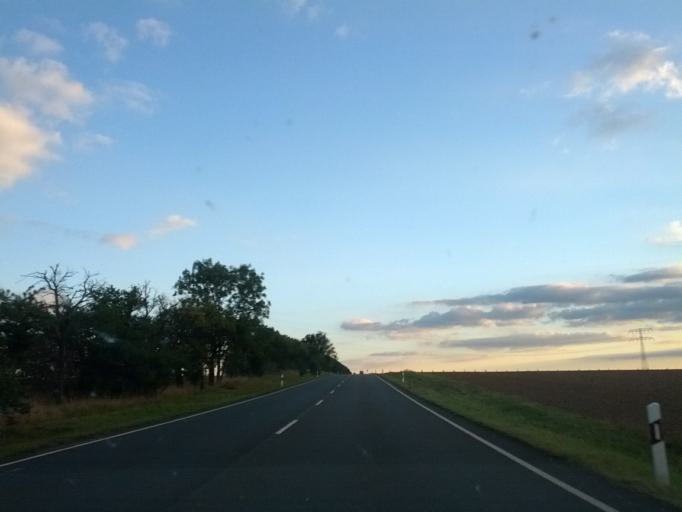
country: DE
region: Thuringia
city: Rockhausen
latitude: 50.9301
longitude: 11.0395
